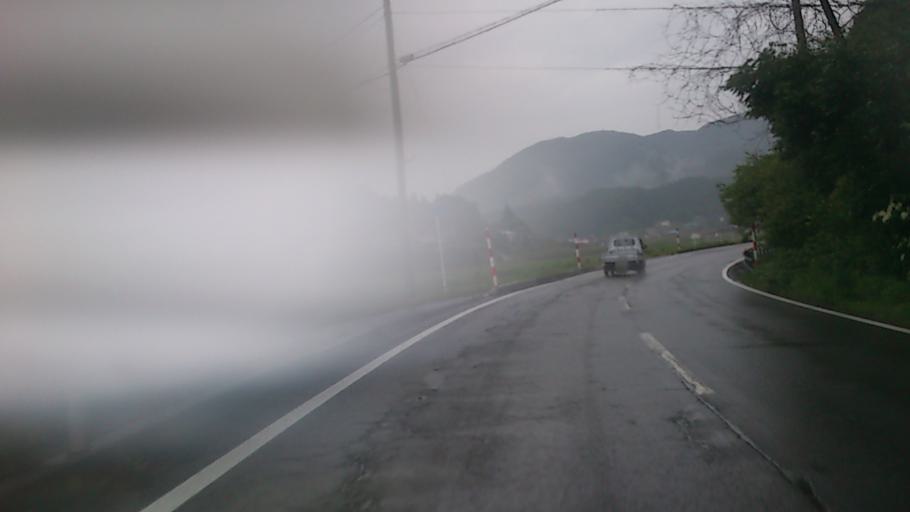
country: JP
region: Akita
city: Takanosu
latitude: 40.2958
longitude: 140.2776
